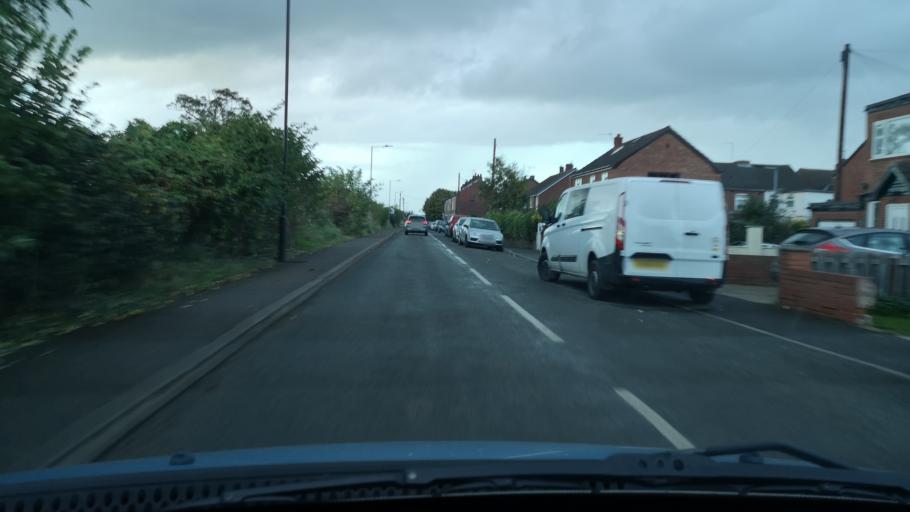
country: GB
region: England
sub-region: Doncaster
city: Norton
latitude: 53.6301
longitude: -1.1844
